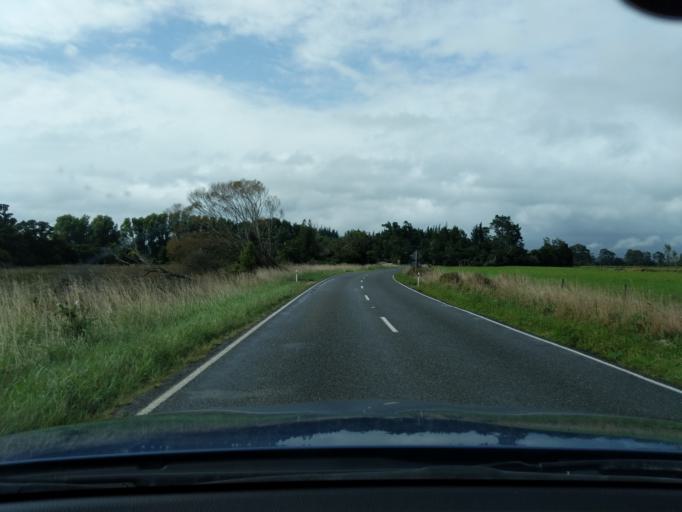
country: NZ
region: Tasman
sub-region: Tasman District
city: Takaka
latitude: -40.6577
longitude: 172.6464
